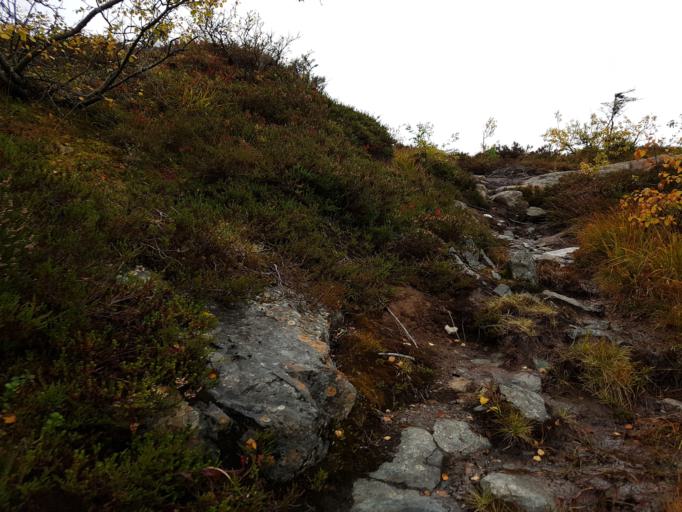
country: NO
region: Sor-Trondelag
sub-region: Melhus
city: Melhus
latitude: 63.4159
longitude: 10.2193
